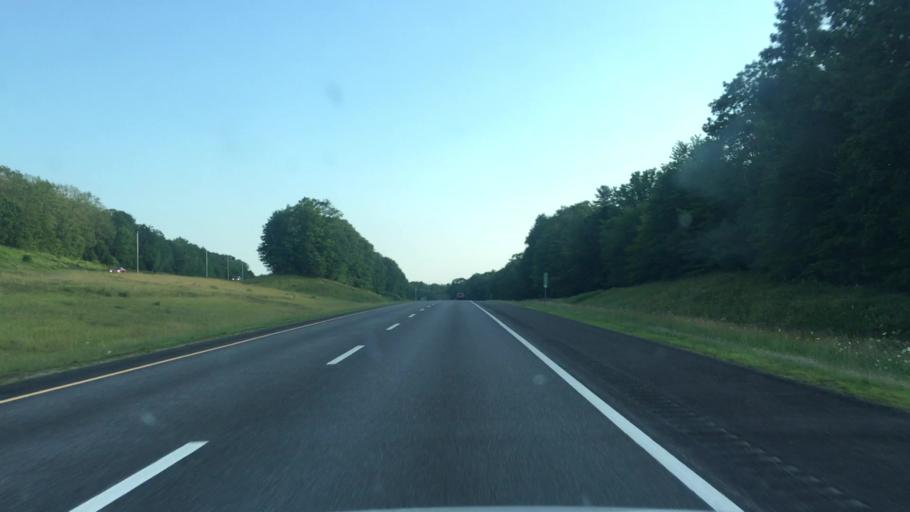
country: US
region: Maine
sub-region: Kennebec County
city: Gardiner
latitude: 44.1890
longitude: -69.8303
